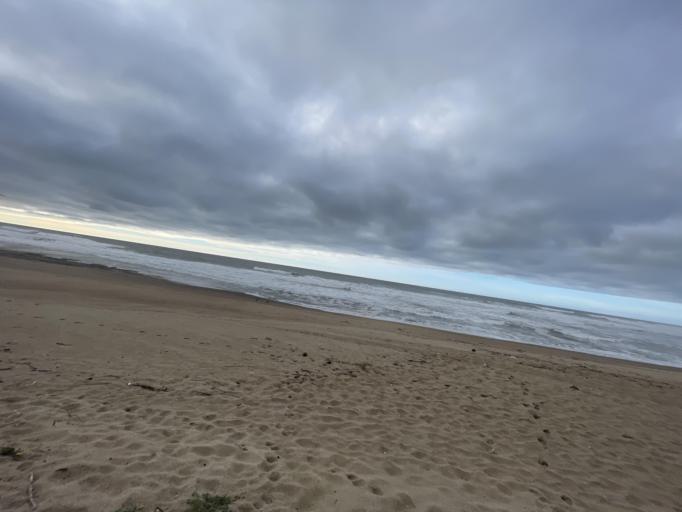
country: PT
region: Porto
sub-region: Vila Nova de Gaia
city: Arcozelo
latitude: 41.0318
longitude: -8.6459
